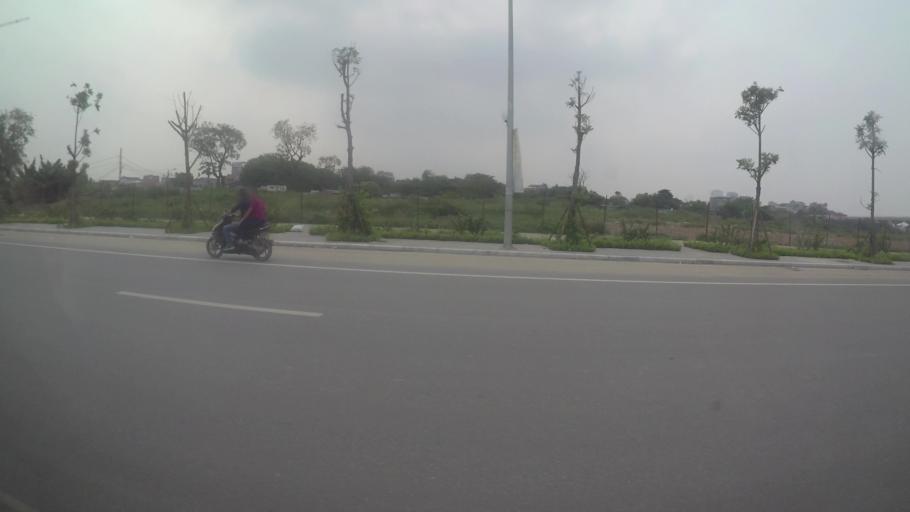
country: VN
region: Ha Noi
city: Cau Dien
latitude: 21.0502
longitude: 105.7355
